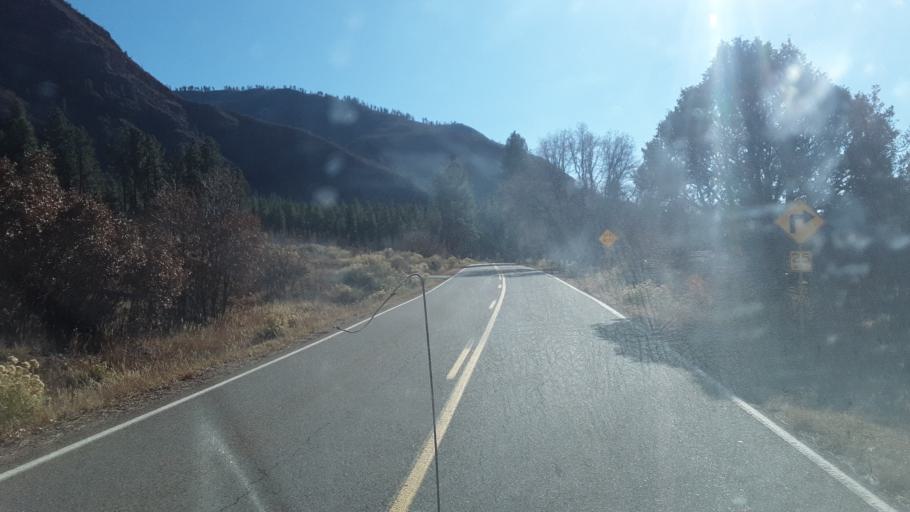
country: US
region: Colorado
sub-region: La Plata County
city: Durango
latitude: 37.4029
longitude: -107.8164
